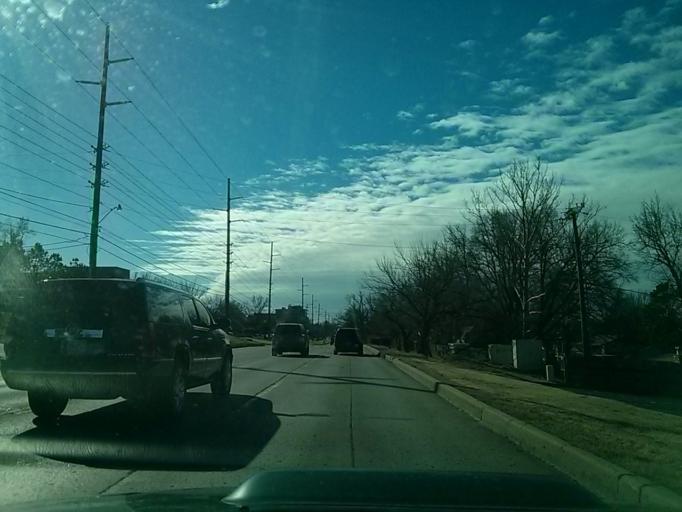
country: US
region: Oklahoma
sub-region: Tulsa County
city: Jenks
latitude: 36.0866
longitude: -95.9581
